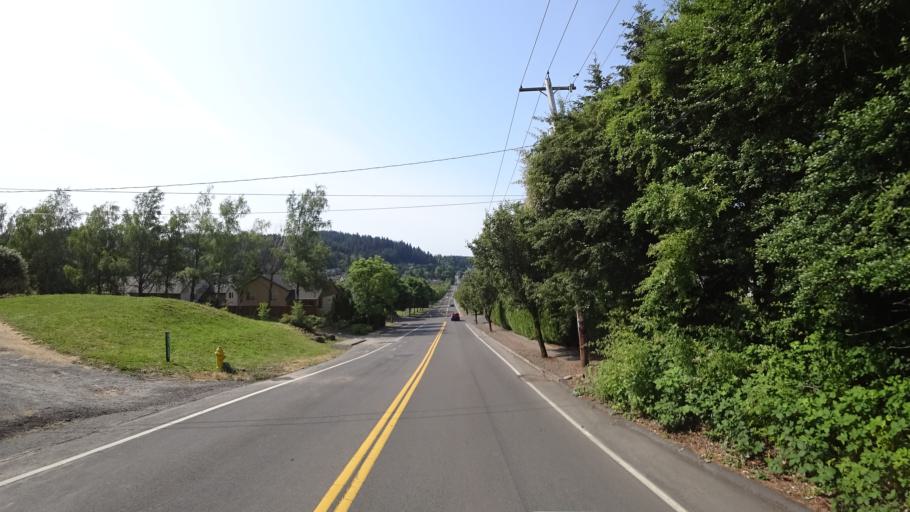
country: US
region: Oregon
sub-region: Clackamas County
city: Happy Valley
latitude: 45.4575
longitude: -122.5142
